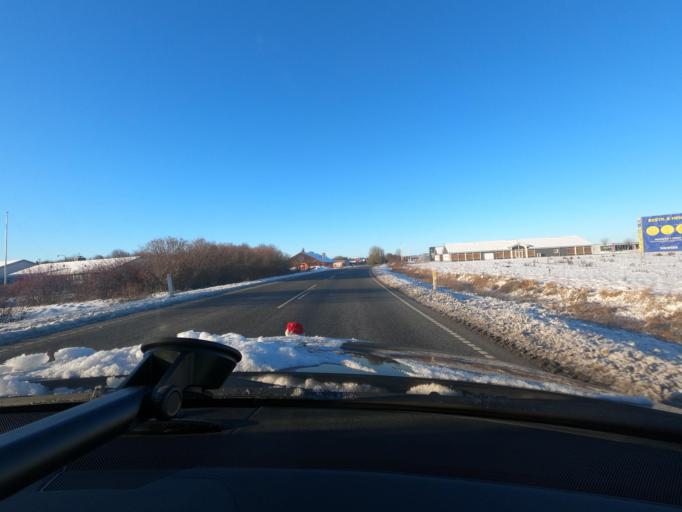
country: DK
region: South Denmark
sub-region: Aabenraa Kommune
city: Rodekro
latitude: 55.0710
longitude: 9.3496
